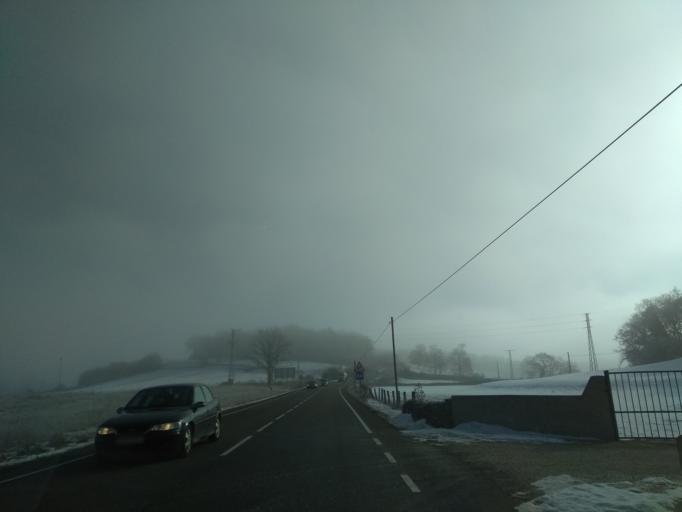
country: ES
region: Castille and Leon
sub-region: Provincia de Burgos
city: Espinosa de los Monteros
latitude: 43.0713
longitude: -3.5274
